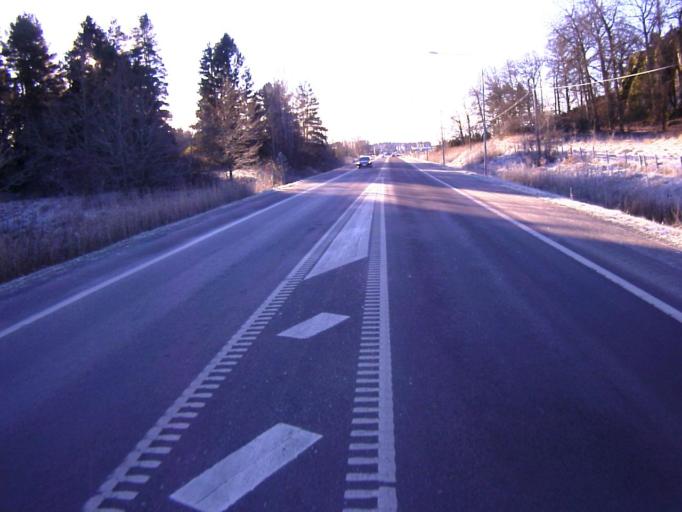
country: SE
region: Soedermanland
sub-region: Eskilstuna Kommun
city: Torshalla
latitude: 59.3996
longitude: 16.4720
